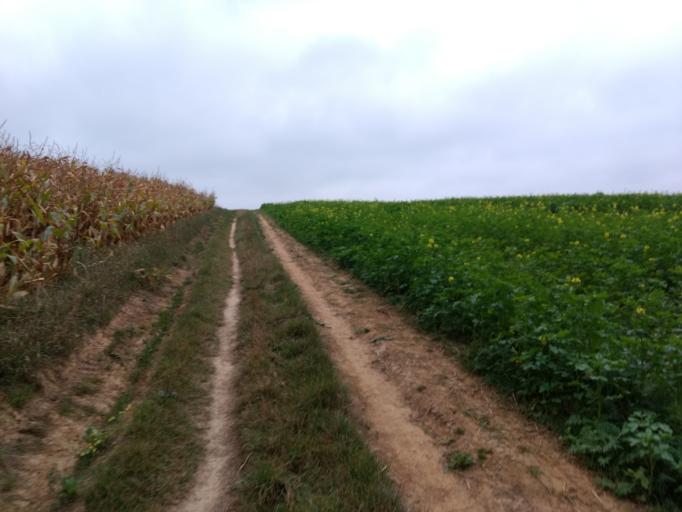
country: BE
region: Flanders
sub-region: Provincie Vlaams-Brabant
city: Bertem
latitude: 50.8769
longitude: 4.6477
